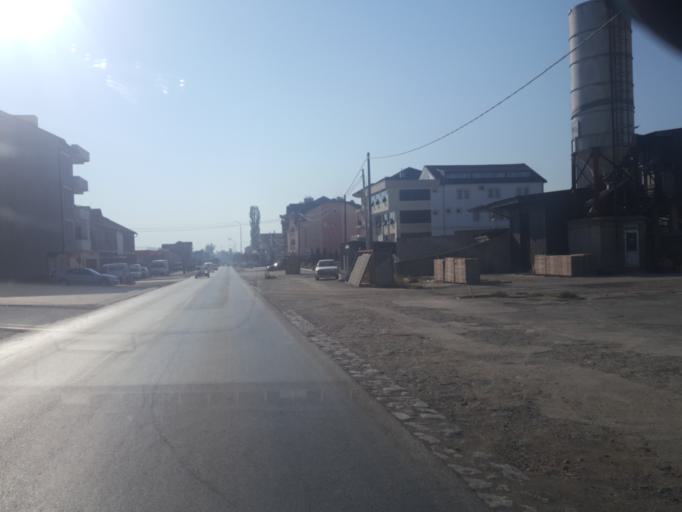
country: XK
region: Gjakova
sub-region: Komuna e Gjakoves
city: Gjakove
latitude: 42.4047
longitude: 20.4106
